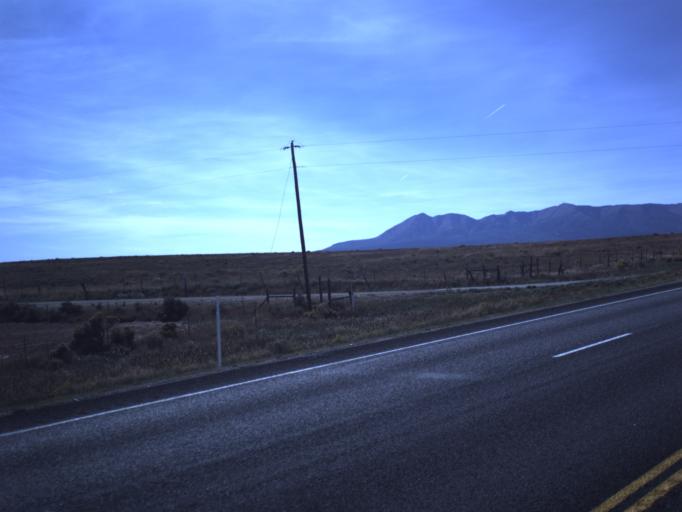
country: US
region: Utah
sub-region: San Juan County
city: Monticello
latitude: 37.8644
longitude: -109.2266
